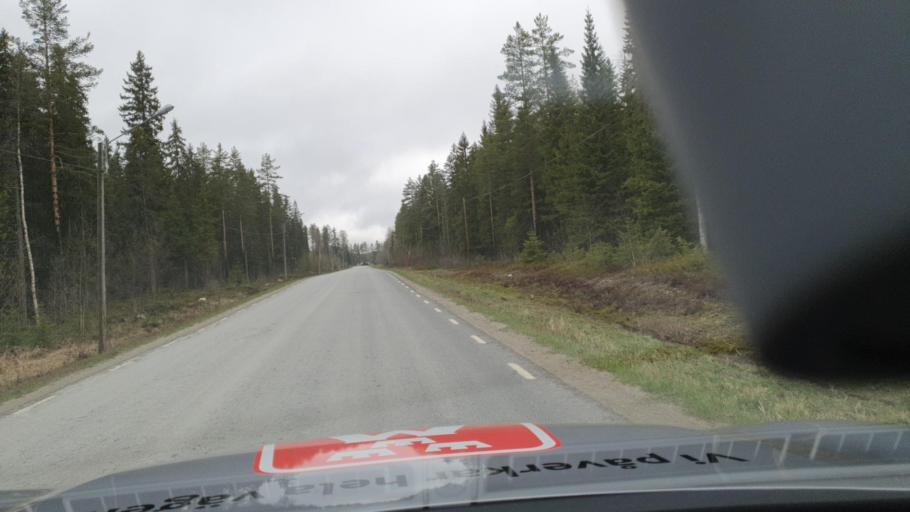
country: SE
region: Vaesternorrland
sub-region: OErnskoeldsviks Kommun
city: Husum
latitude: 63.5863
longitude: 19.0210
